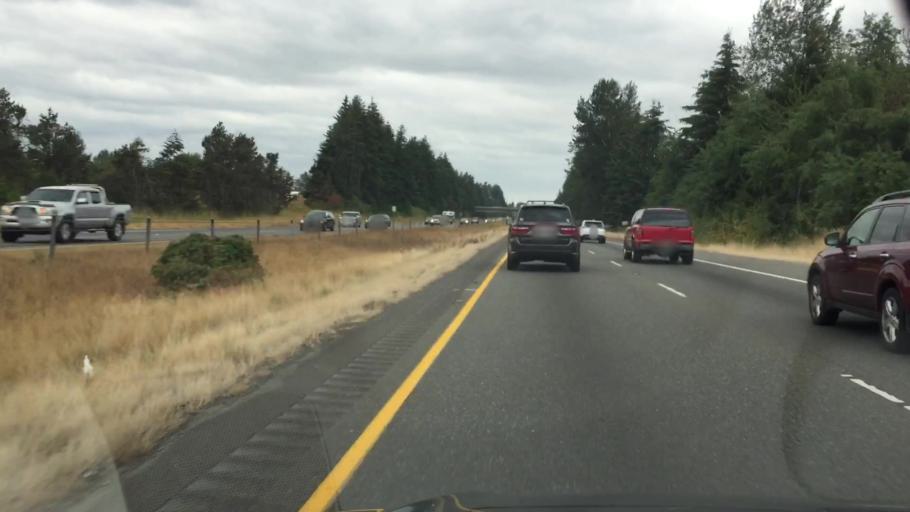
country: US
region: Washington
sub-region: Pierce County
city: Summit
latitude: 47.1587
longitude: -122.3716
